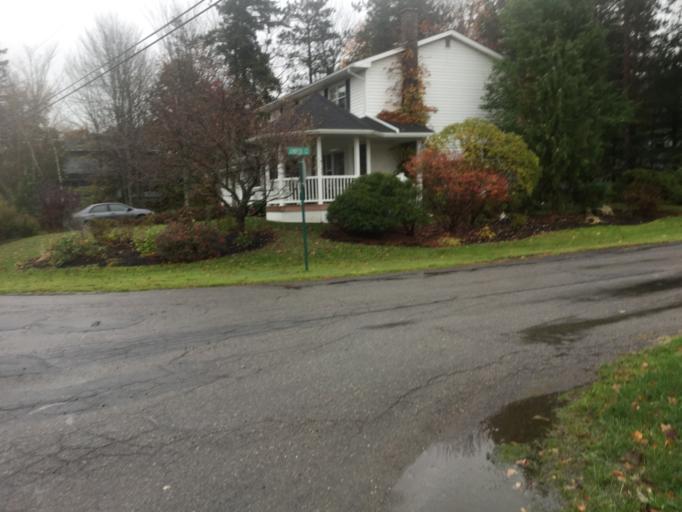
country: CA
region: Nova Scotia
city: New Glasgow
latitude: 45.5487
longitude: -62.6773
